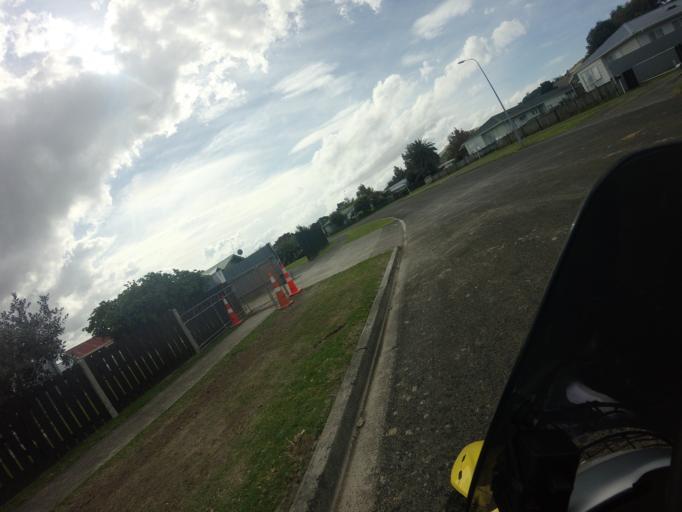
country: NZ
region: Gisborne
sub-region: Gisborne District
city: Gisborne
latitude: -38.6774
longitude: 178.0522
